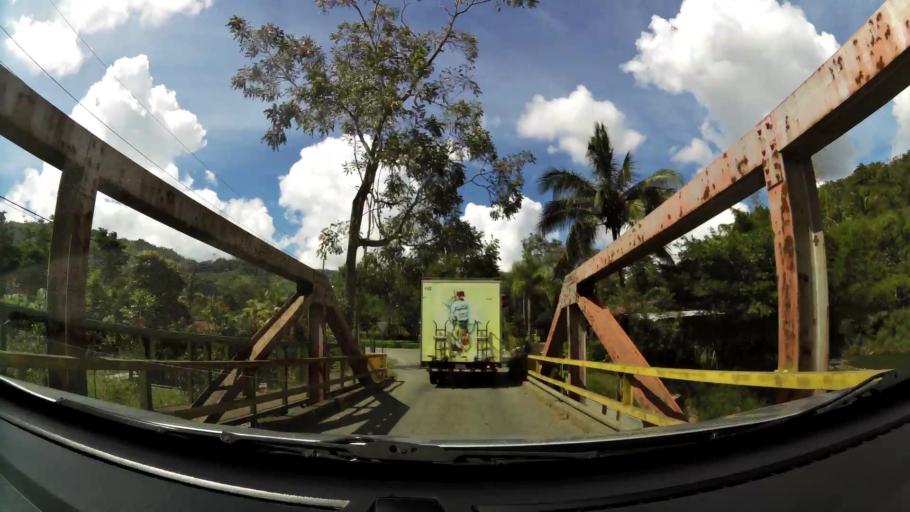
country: CR
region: San Jose
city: San Isidro
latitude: 9.3526
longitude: -83.7280
